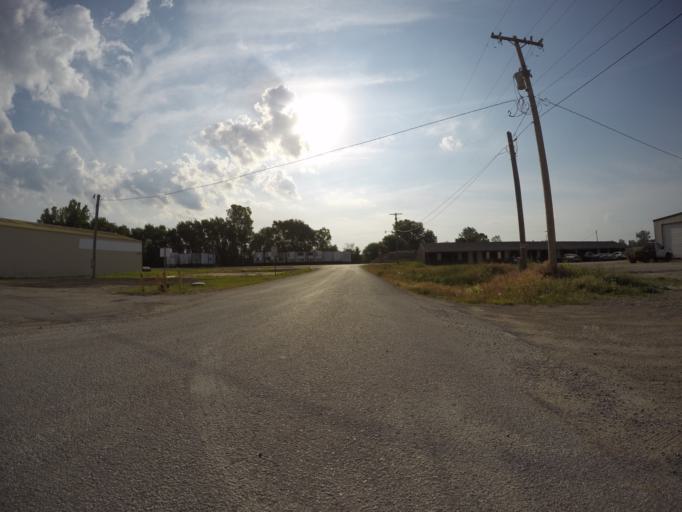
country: US
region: Kansas
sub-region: Doniphan County
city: Elwood
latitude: 39.7520
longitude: -94.8688
